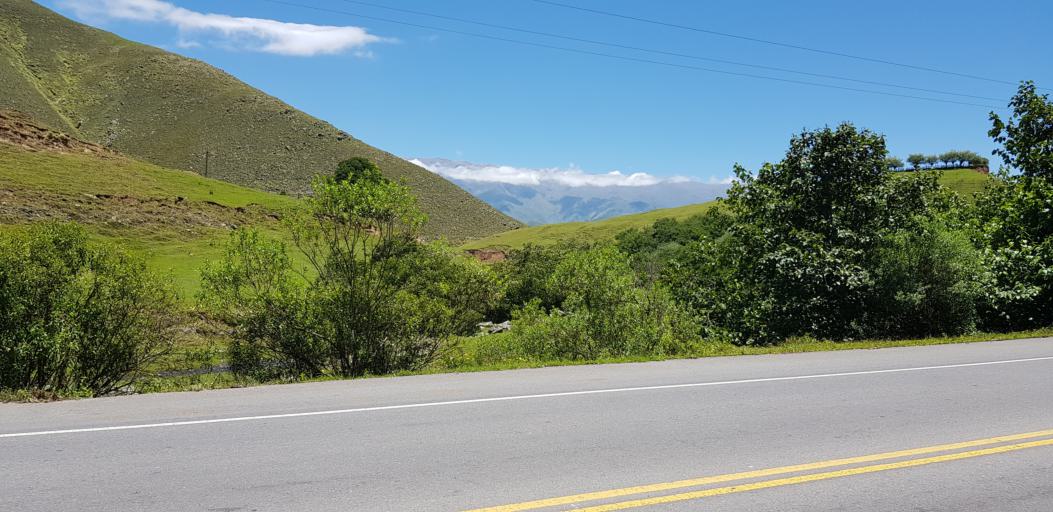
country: AR
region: Tucuman
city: Tafi del Valle
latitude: -26.9475
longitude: -65.6647
